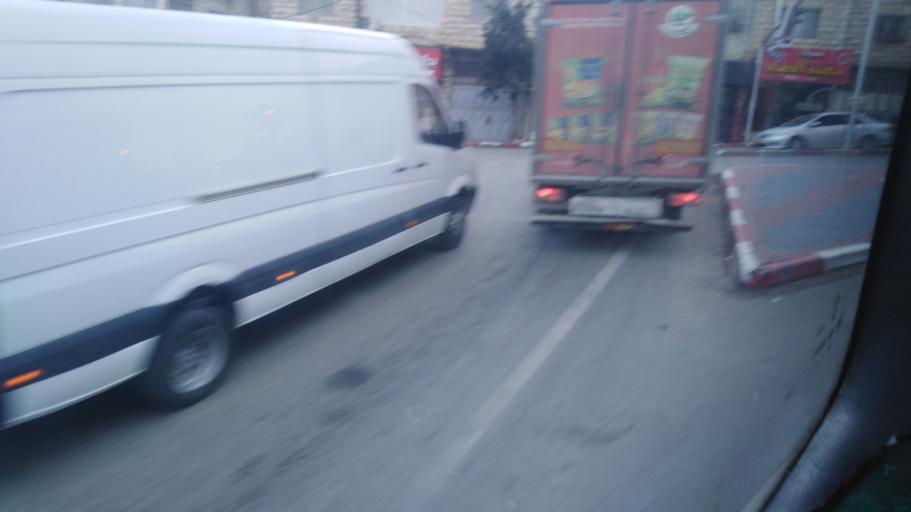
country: PS
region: West Bank
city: Hebron
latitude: 31.5265
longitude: 35.0874
